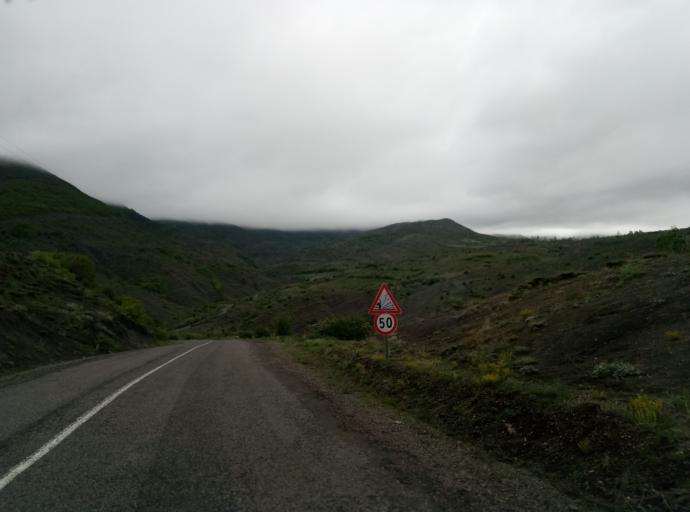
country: TR
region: Sivas
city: Koyulhisar
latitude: 40.1734
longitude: 37.9029
